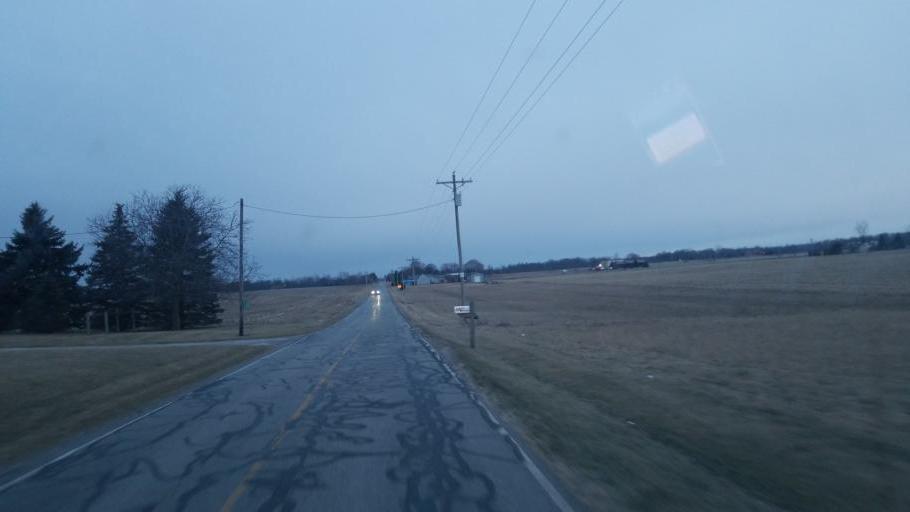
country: US
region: Ohio
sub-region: Defiance County
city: Hicksville
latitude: 41.3250
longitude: -84.7423
